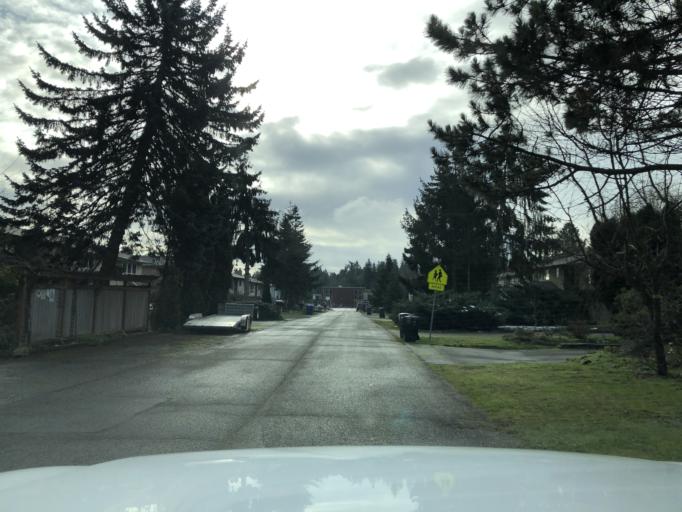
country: US
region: Washington
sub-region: King County
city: Lake Forest Park
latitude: 47.7261
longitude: -122.3050
